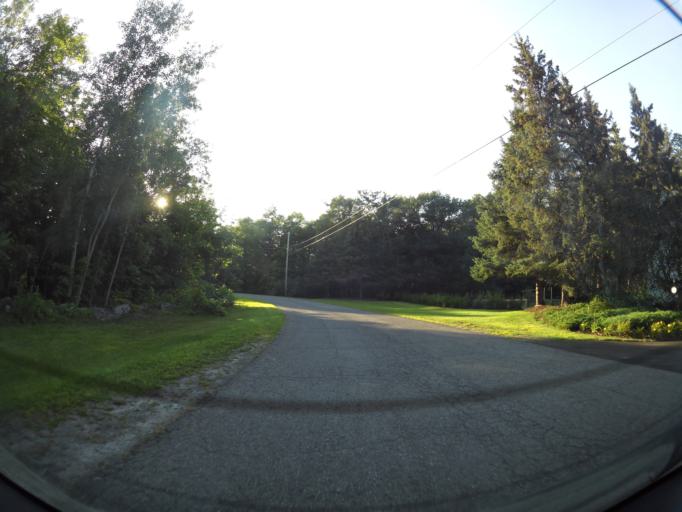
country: CA
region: Ontario
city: Clarence-Rockland
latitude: 45.5066
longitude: -75.4153
